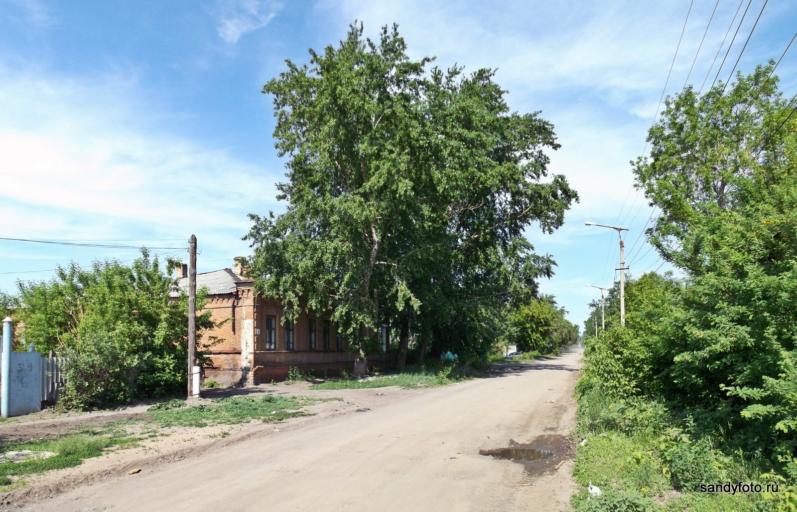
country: RU
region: Chelyabinsk
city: Troitsk
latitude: 54.0773
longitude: 61.5473
